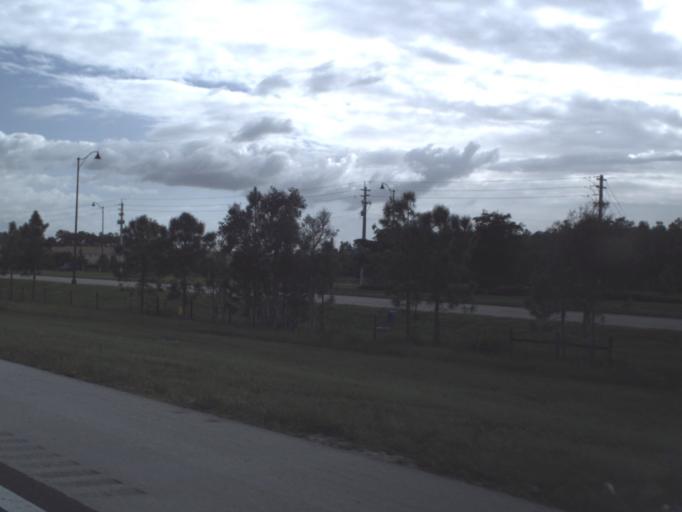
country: US
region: Florida
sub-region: Lee County
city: Bonita Springs
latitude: 26.3761
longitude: -81.7723
